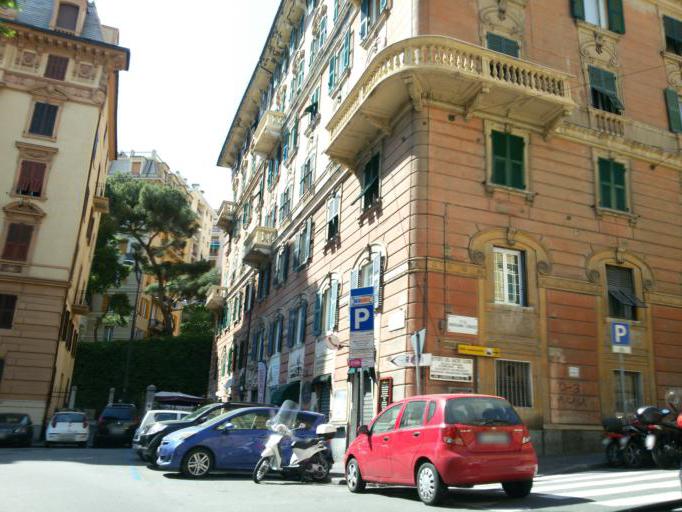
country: IT
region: Liguria
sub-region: Provincia di Genova
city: Genoa
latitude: 44.4211
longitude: 8.9303
